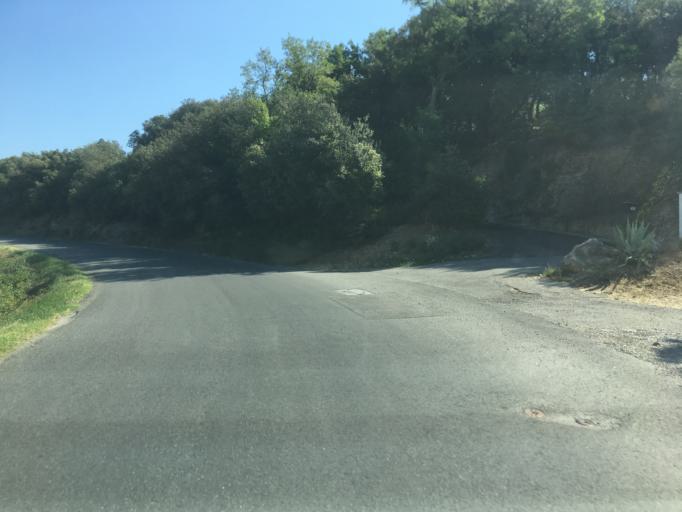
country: FR
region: Provence-Alpes-Cote d'Azur
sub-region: Departement des Alpes-de-Haute-Provence
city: Oraison
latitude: 43.8846
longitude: 5.9148
